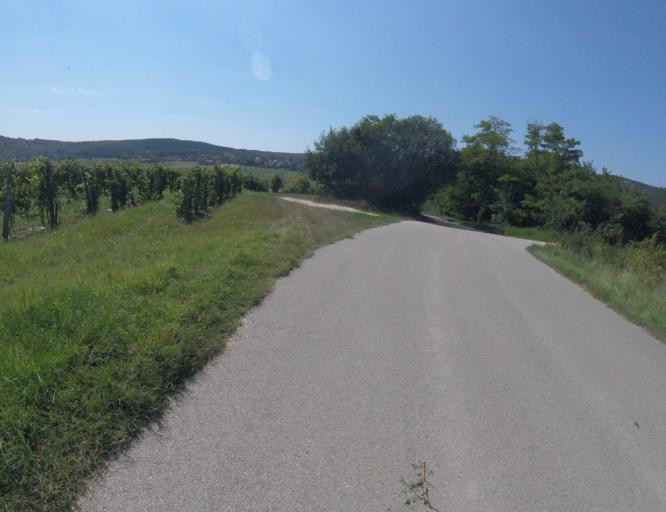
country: HU
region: Fejer
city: Velence
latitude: 47.2619
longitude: 18.6290
